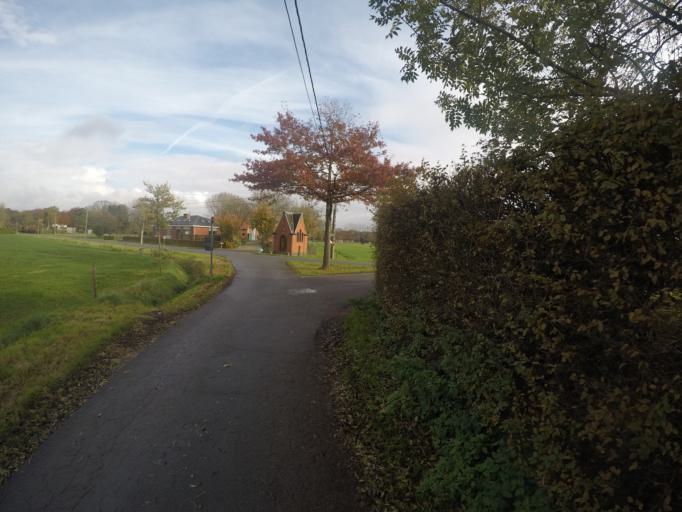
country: BE
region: Flanders
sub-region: Provincie Oost-Vlaanderen
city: Temse
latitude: 51.1636
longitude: 4.1894
